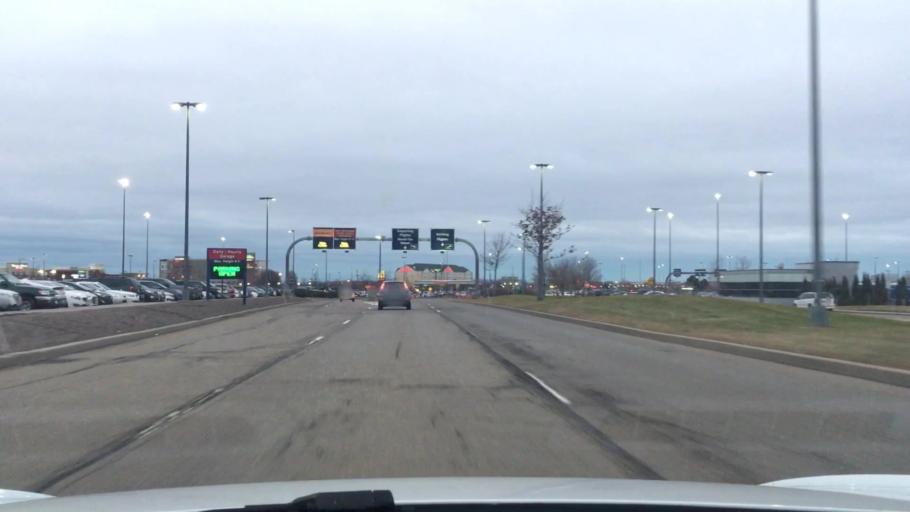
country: US
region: New York
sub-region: Erie County
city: Williamsville
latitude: 42.9342
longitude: -78.7271
